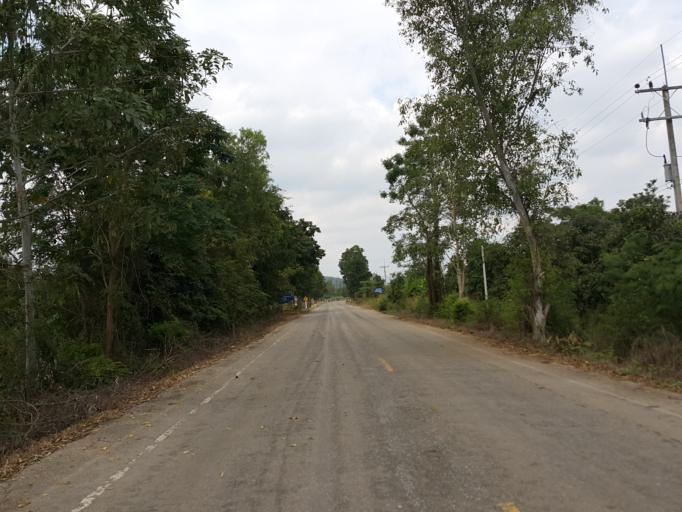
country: TH
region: Sukhothai
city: Thung Saliam
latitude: 17.3786
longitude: 99.5885
